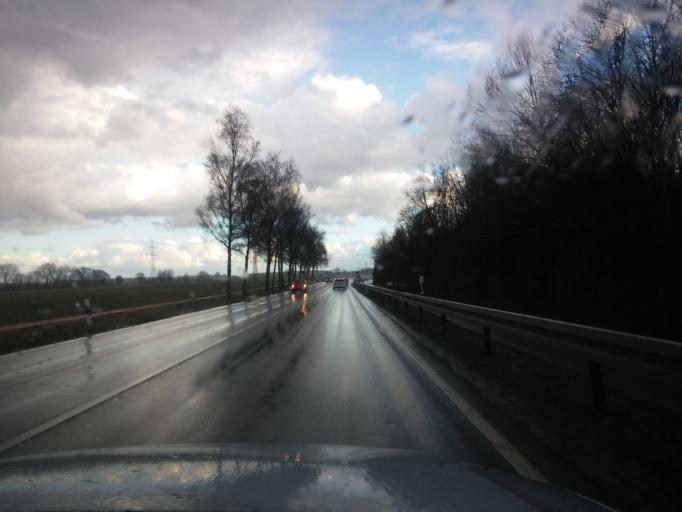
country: DE
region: Bavaria
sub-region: Upper Bavaria
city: Ismaning
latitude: 48.2033
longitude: 11.7015
